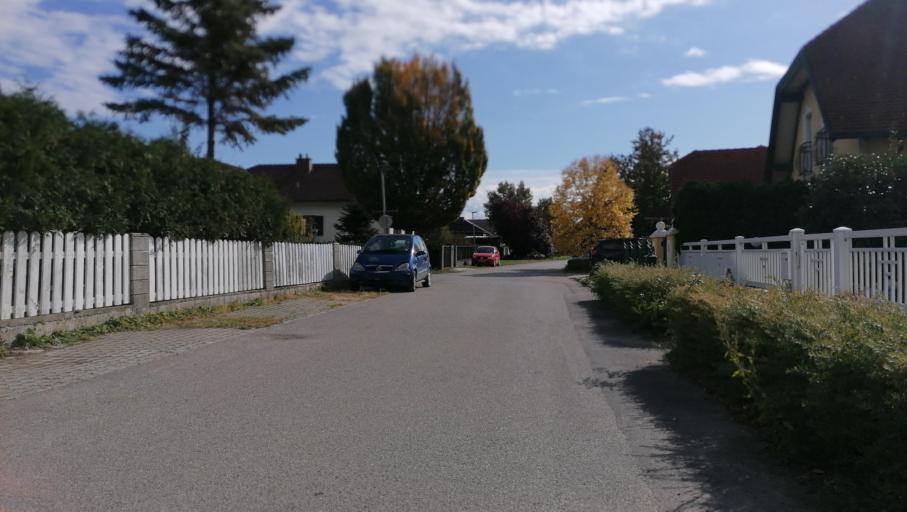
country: AT
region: Lower Austria
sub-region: Politischer Bezirk Baden
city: Tattendorf
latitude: 47.9615
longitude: 16.2984
